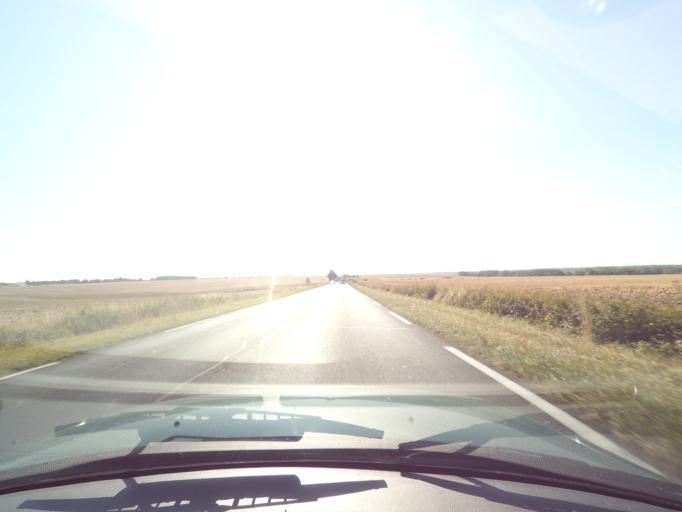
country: FR
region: Poitou-Charentes
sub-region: Departement de la Vienne
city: Ayron
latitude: 46.6552
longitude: 0.1080
